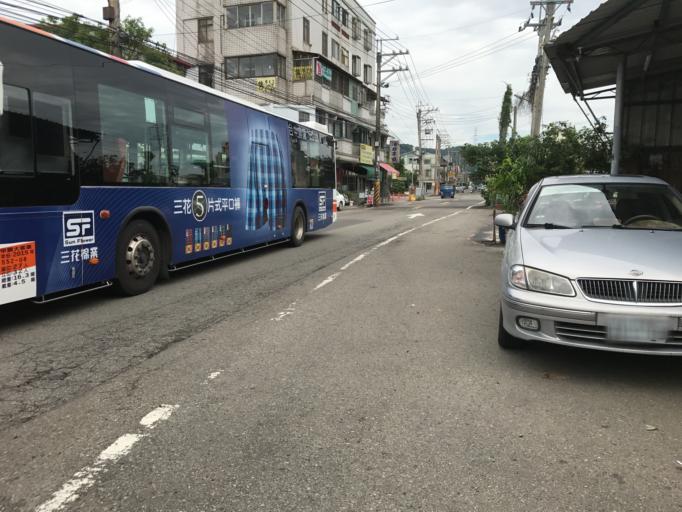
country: TW
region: Taiwan
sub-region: Taichung City
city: Taichung
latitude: 24.0850
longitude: 120.7085
